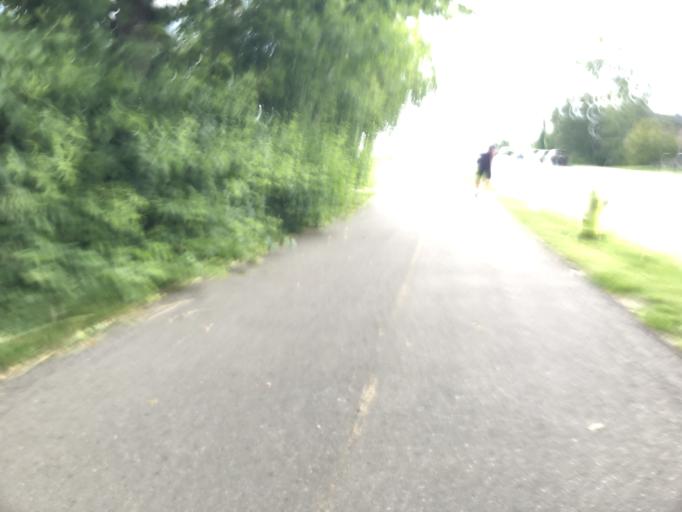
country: CA
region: Alberta
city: Calgary
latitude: 51.0337
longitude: -114.0135
